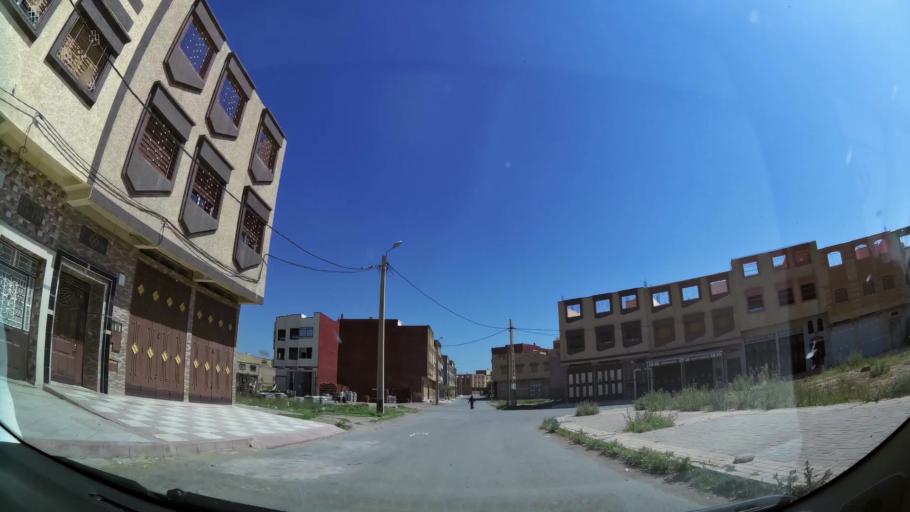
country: MA
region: Oriental
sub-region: Oujda-Angad
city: Oujda
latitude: 34.6898
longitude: -1.9356
